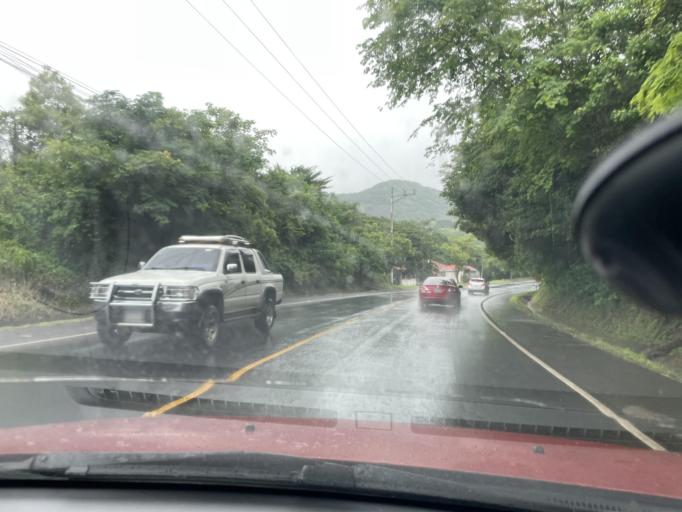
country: SV
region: San Miguel
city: San Miguel
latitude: 13.5501
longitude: -88.1179
